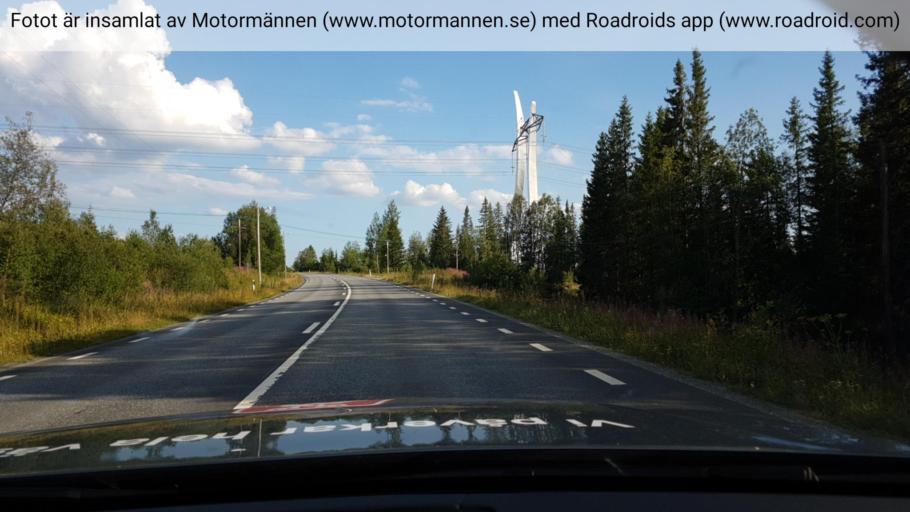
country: SE
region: Jaemtland
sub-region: Are Kommun
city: Are
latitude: 63.3465
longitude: 13.1912
